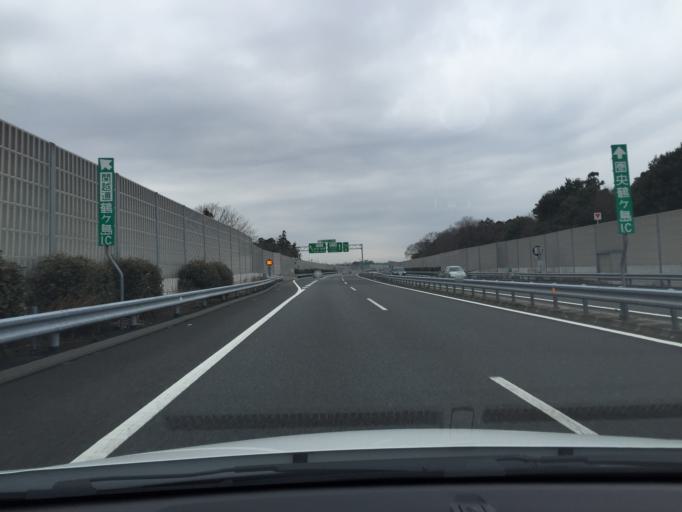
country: JP
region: Saitama
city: Sakado
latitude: 35.9393
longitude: 139.4102
